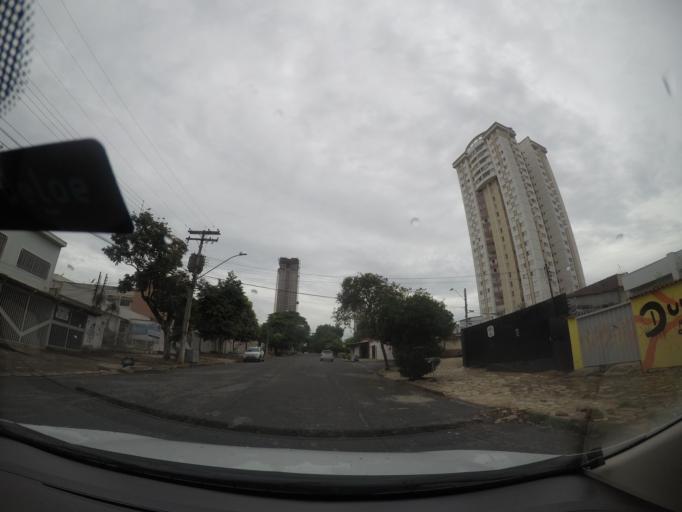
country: BR
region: Goias
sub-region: Goiania
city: Goiania
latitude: -16.6818
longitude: -49.2450
